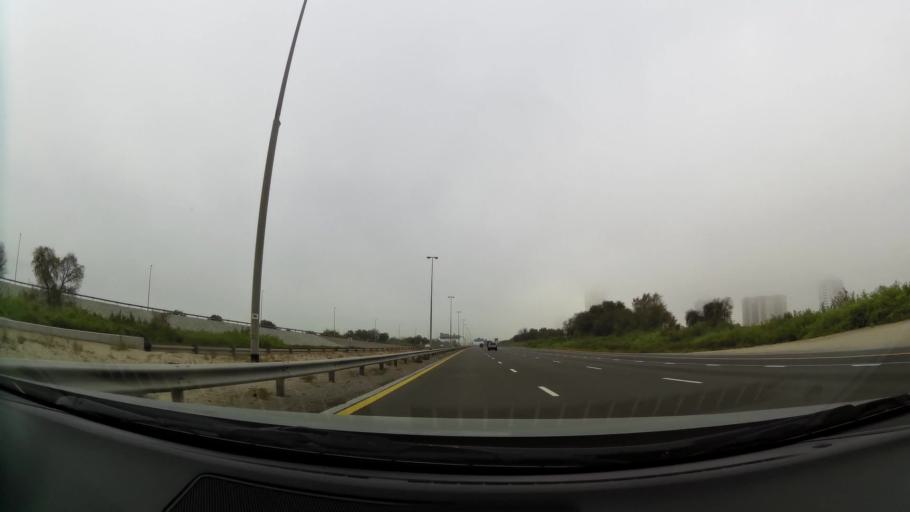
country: AE
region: Dubai
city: Dubai
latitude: 25.1019
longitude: 55.3802
